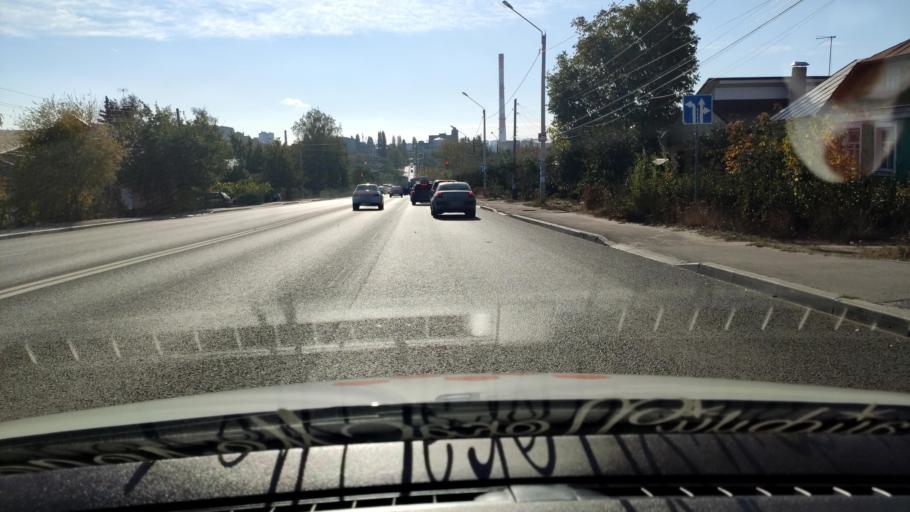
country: RU
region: Voronezj
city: Voronezh
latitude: 51.6952
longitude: 39.1569
